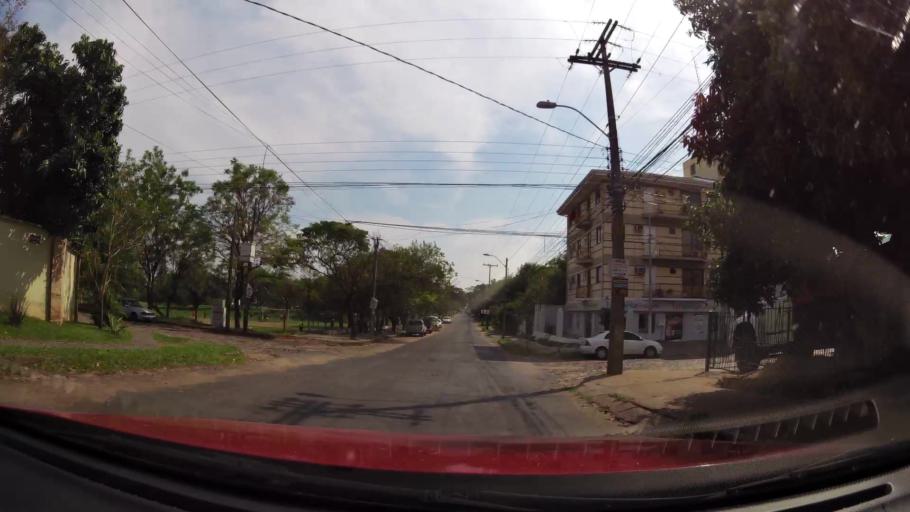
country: PY
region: Central
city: Fernando de la Mora
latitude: -25.2662
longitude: -57.5609
